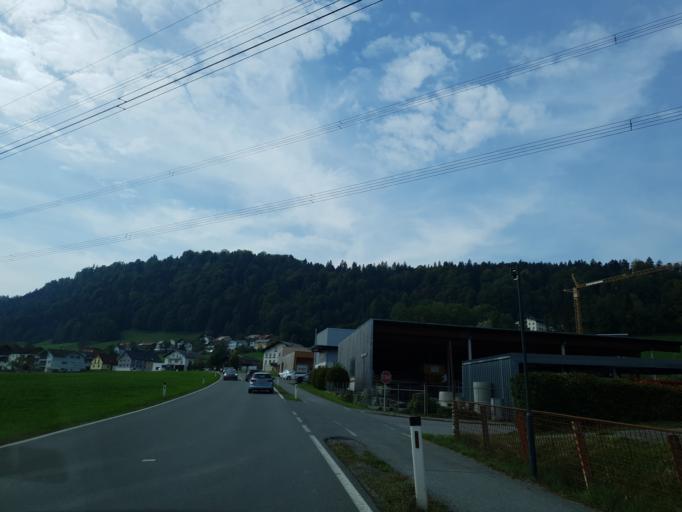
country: AT
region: Vorarlberg
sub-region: Politischer Bezirk Bregenz
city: Doren
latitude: 47.5172
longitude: 9.8487
